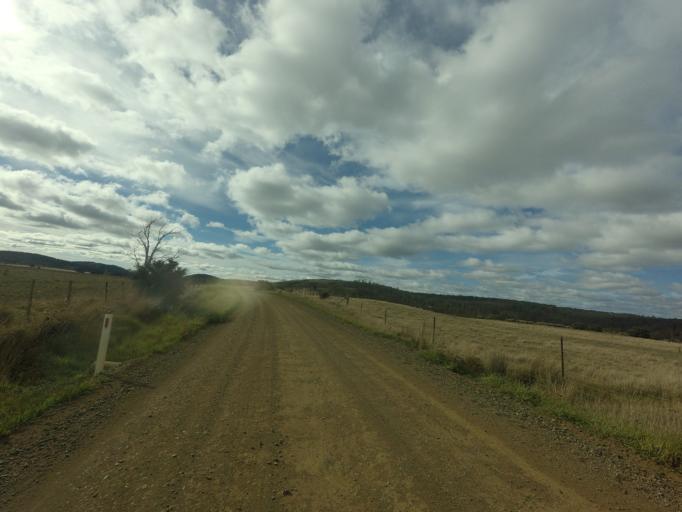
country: AU
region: Tasmania
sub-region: Brighton
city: Bridgewater
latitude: -42.4279
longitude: 147.3894
